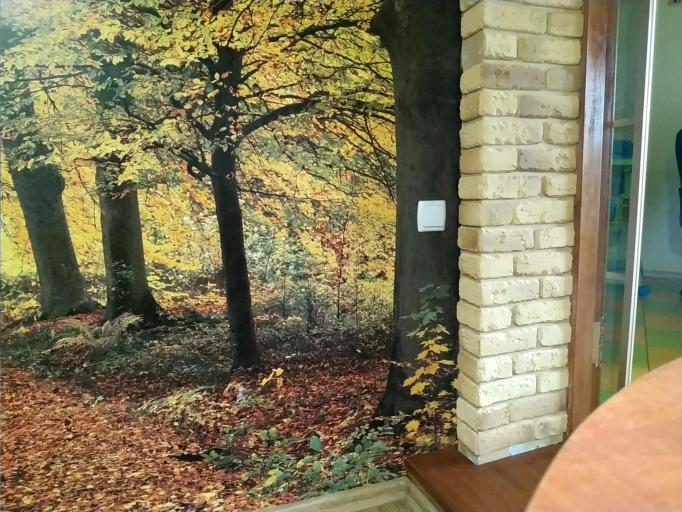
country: RU
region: Smolensk
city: Dorogobuzh
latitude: 54.9653
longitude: 33.2795
